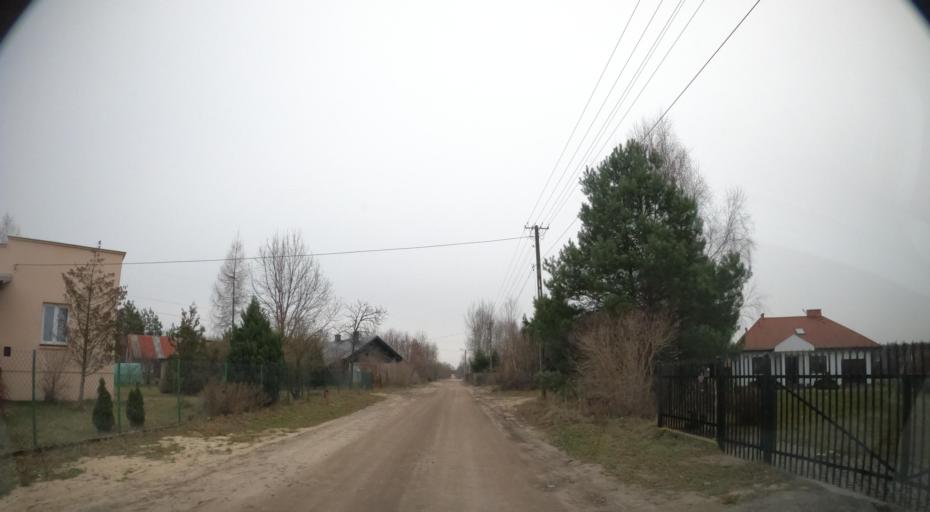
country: PL
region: Masovian Voivodeship
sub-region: Powiat radomski
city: Jastrzebia
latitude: 51.4871
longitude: 21.1887
